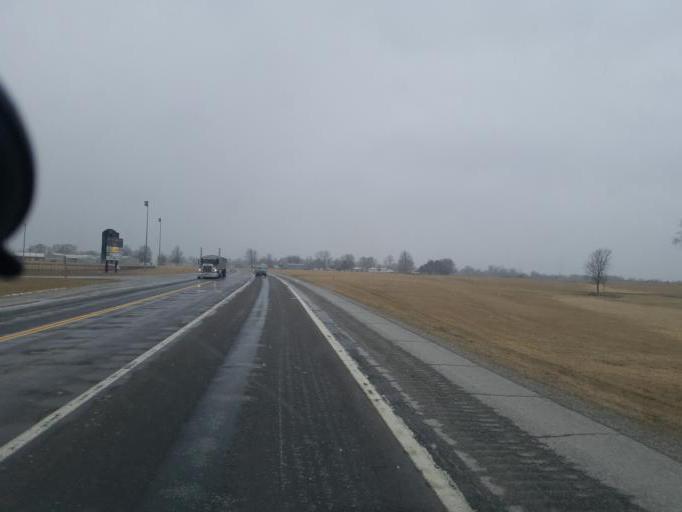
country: US
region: Missouri
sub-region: Schuyler County
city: Lancaster
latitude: 40.4220
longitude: -92.5683
